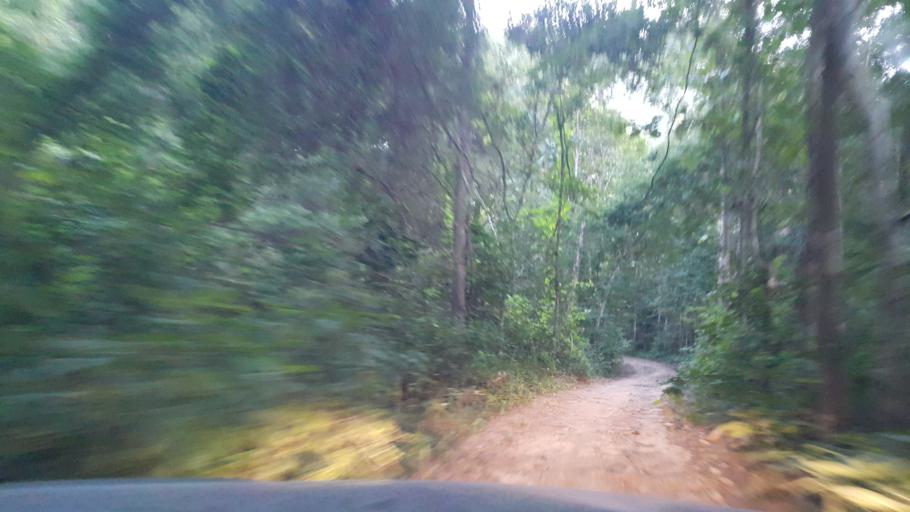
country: TH
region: Lamphun
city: Ban Thi
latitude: 18.6820
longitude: 99.2044
